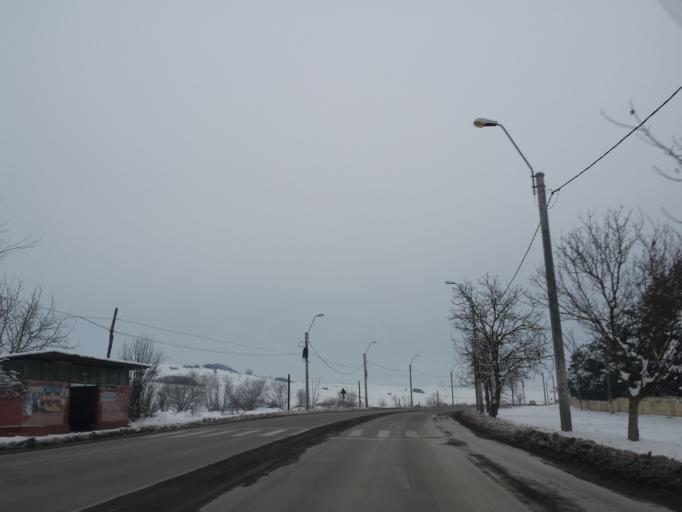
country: RO
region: Hunedoara
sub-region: Municipiul Deva
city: Cristur
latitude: 45.8427
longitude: 22.9479
